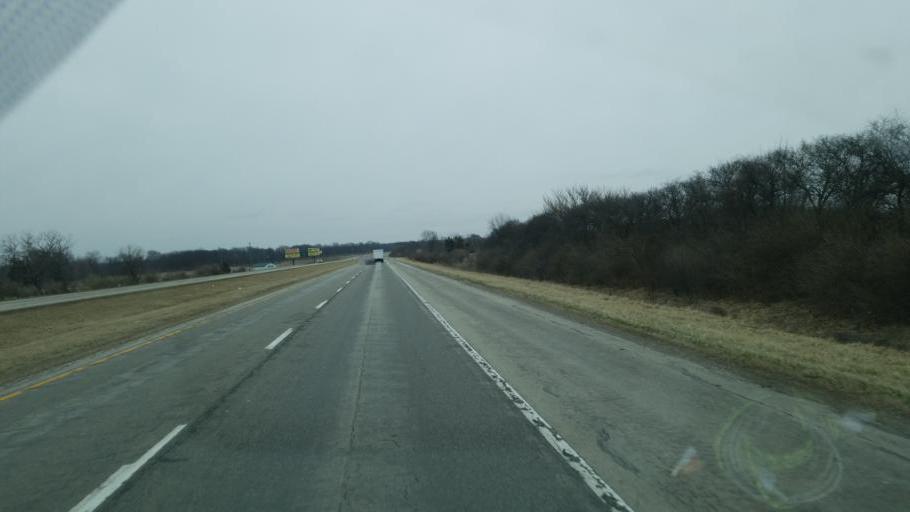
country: US
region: Indiana
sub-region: Fulton County
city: Rochester
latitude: 41.0363
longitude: -86.1921
